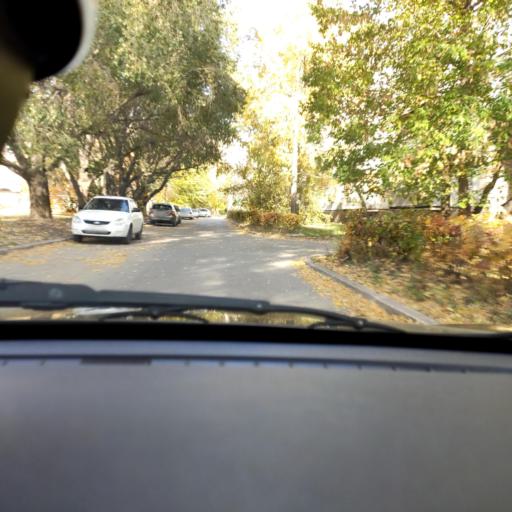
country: RU
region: Samara
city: Tol'yatti
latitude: 53.5309
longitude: 49.2699
